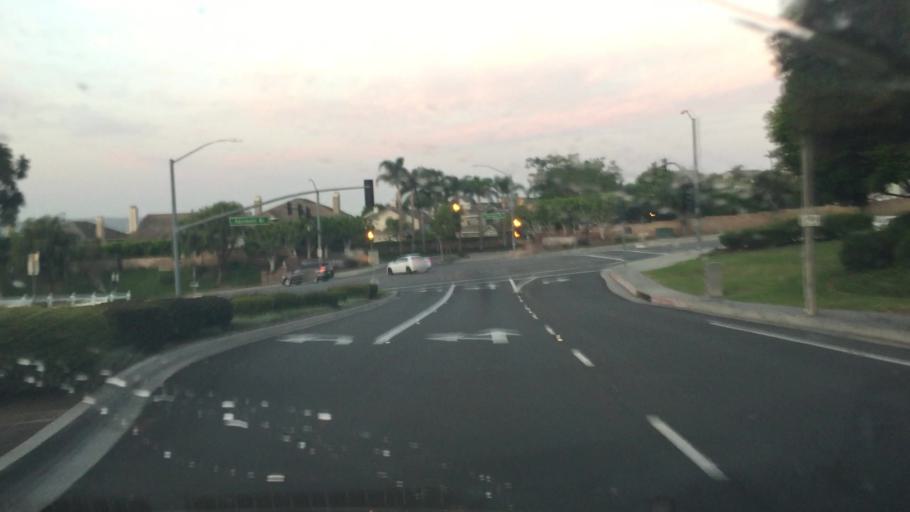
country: US
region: California
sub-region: Orange County
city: Yorba Linda
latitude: 33.8714
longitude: -117.7800
